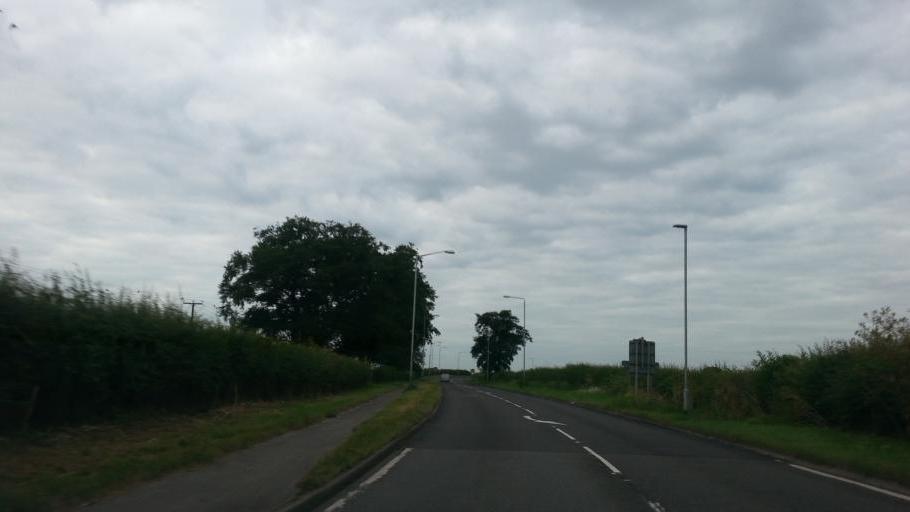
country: GB
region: England
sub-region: Nottinghamshire
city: Farndon
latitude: 53.0377
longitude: -0.8784
